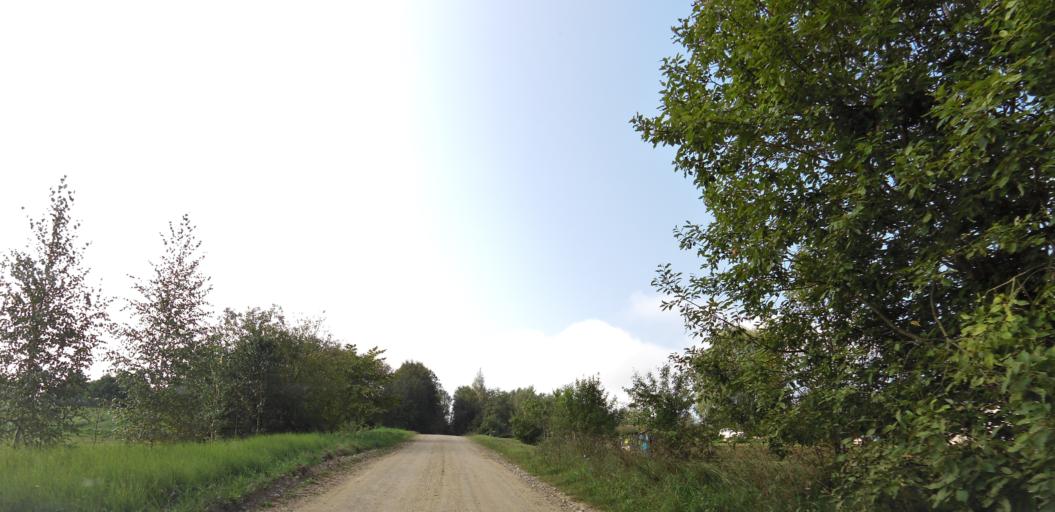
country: LT
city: Grigiskes
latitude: 54.7738
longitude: 25.0616
